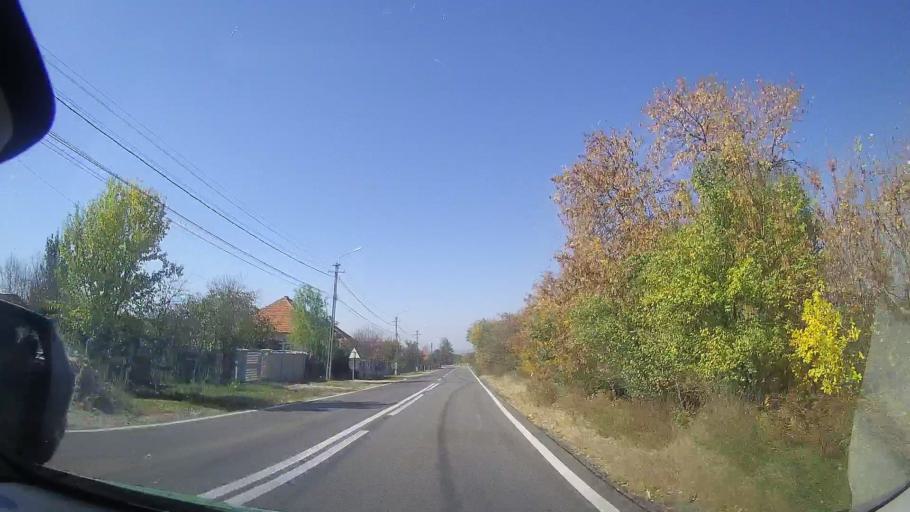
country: RO
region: Timis
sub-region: Municipiul Lugoj
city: Lugoj
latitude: 45.7038
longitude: 21.9614
